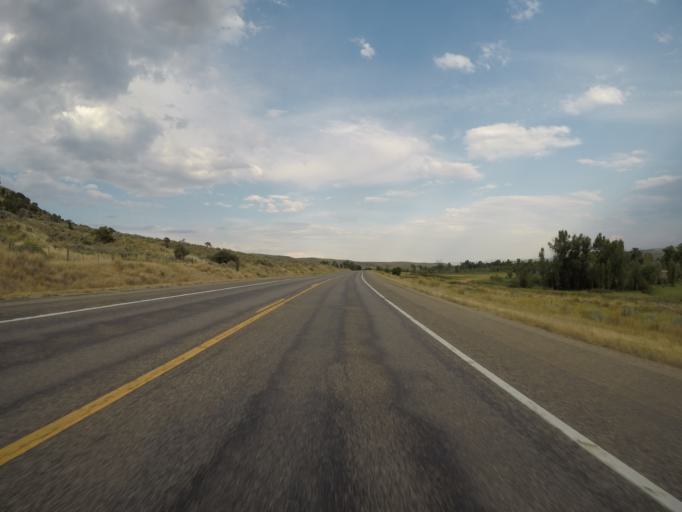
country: US
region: Colorado
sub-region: Moffat County
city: Craig
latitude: 40.5256
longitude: -107.4107
